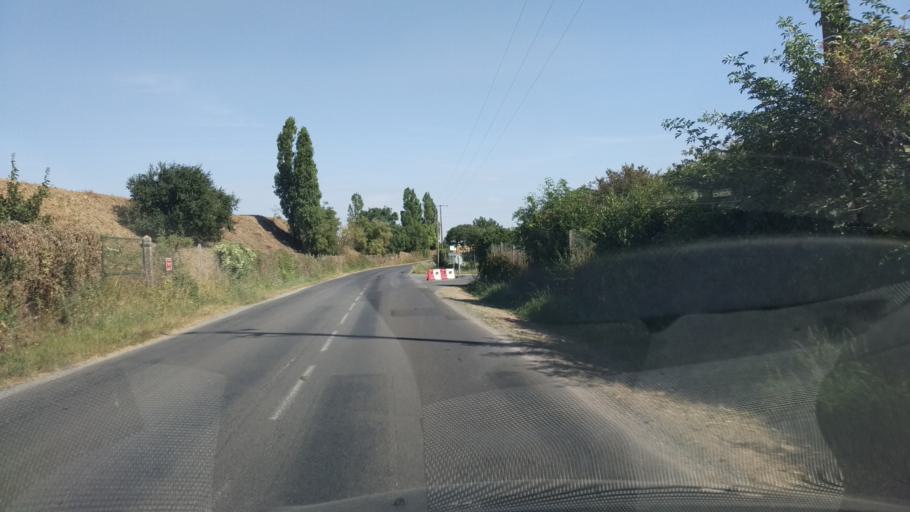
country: FR
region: Poitou-Charentes
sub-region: Departement de la Vienne
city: Cisse
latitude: 46.6620
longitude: 0.2083
